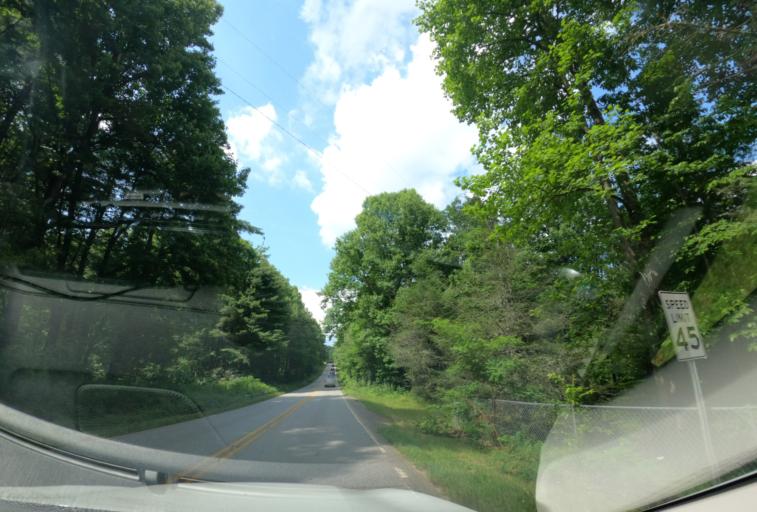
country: US
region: South Carolina
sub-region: Oconee County
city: Walhalla
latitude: 35.0623
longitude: -83.0073
